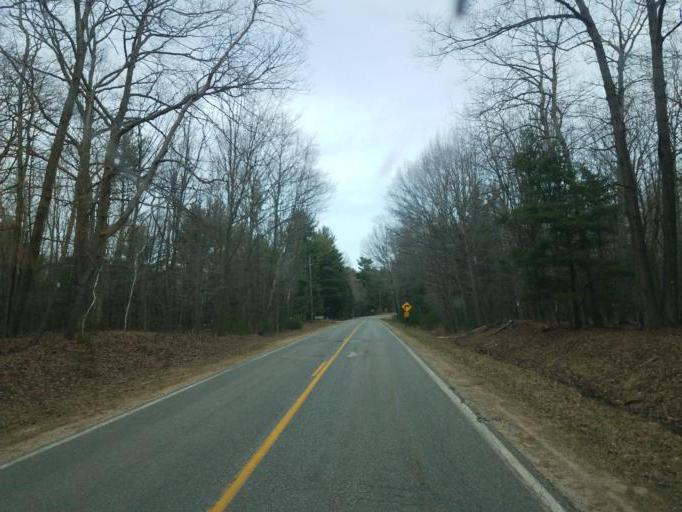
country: US
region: Michigan
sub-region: Oceana County
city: Hart
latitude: 43.7423
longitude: -86.4588
